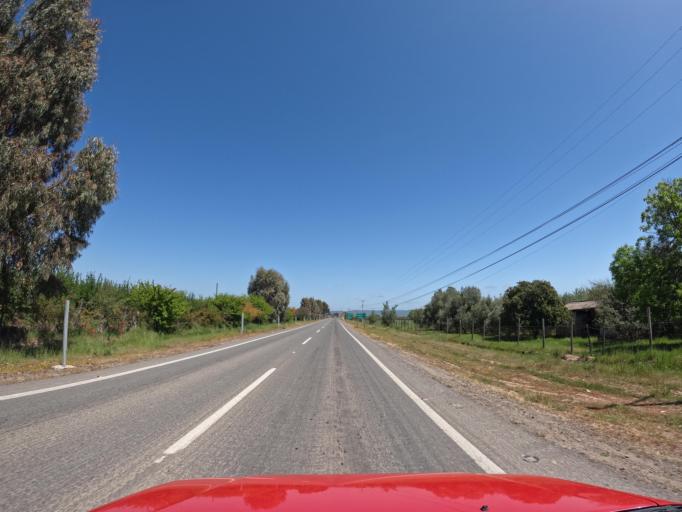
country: CL
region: O'Higgins
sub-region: Provincia de Colchagua
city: Santa Cruz
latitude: -34.7343
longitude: -71.6927
